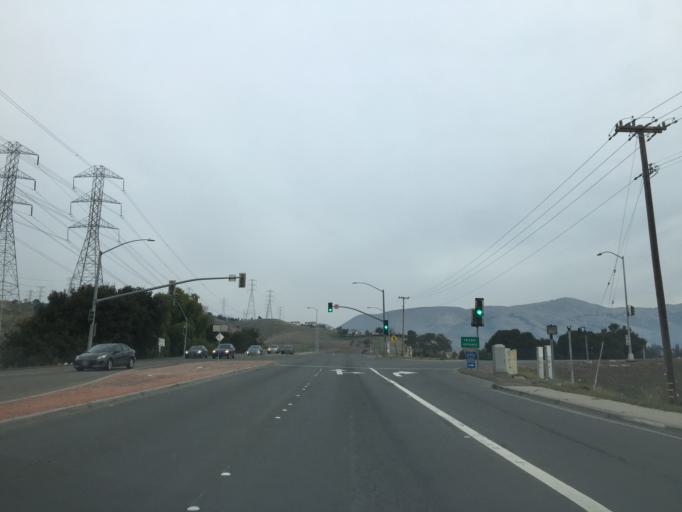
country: US
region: California
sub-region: Alameda County
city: Fremont
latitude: 37.5140
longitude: -121.9419
